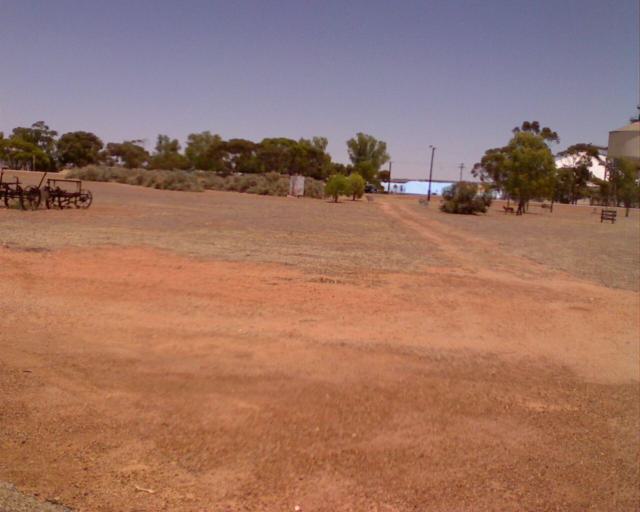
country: AU
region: Western Australia
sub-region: Wongan-Ballidu
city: Wongan Hills
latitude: -30.8288
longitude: 117.4815
